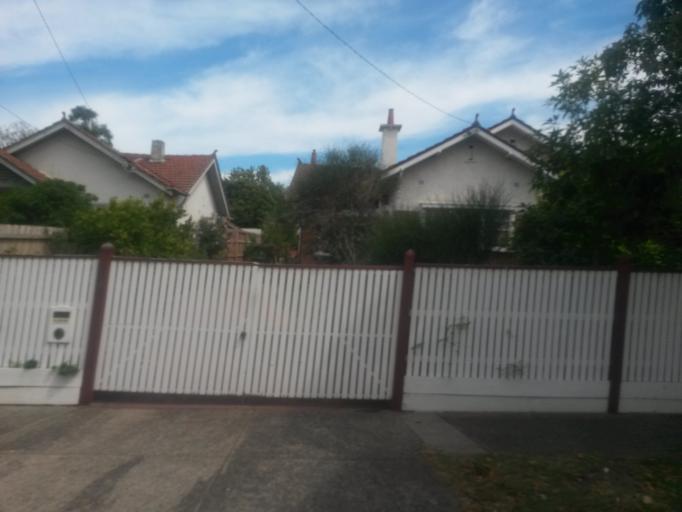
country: AU
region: Victoria
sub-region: Stonnington
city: Glen Iris
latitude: -37.8565
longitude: 145.0545
